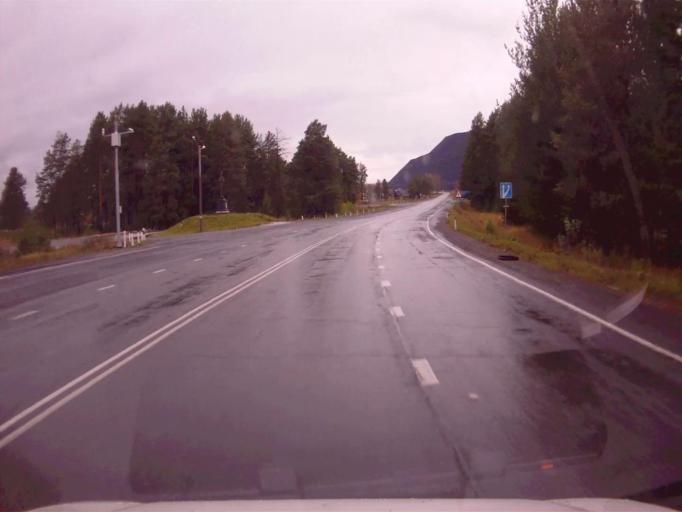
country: RU
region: Chelyabinsk
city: Verkhniy Ufaley
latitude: 56.0281
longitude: 60.2865
